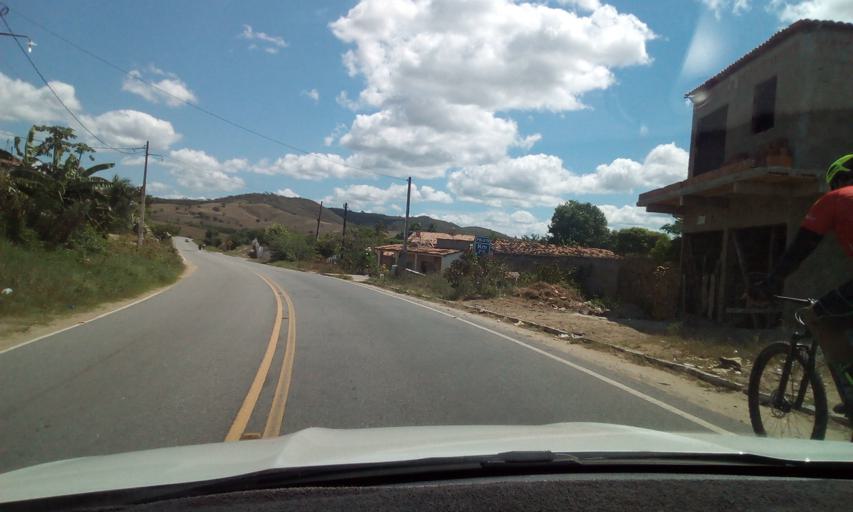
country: BR
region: Paraiba
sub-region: Serra Redonda
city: Alagoa Grande
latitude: -7.1635
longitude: -35.5927
